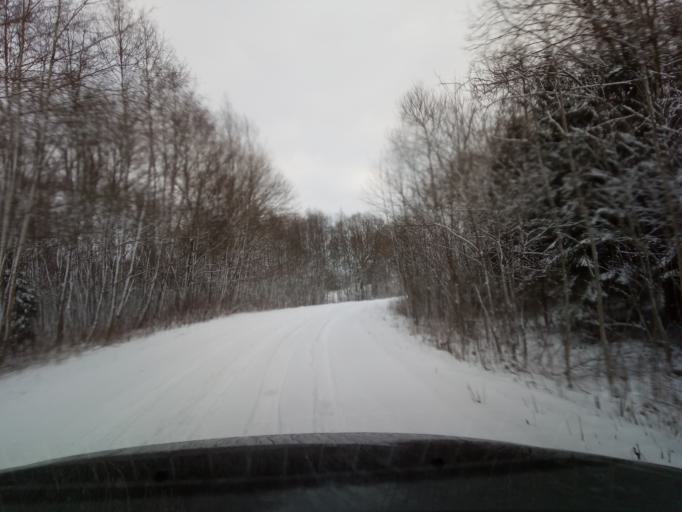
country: LT
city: Zarasai
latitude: 55.7321
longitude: 25.9478
